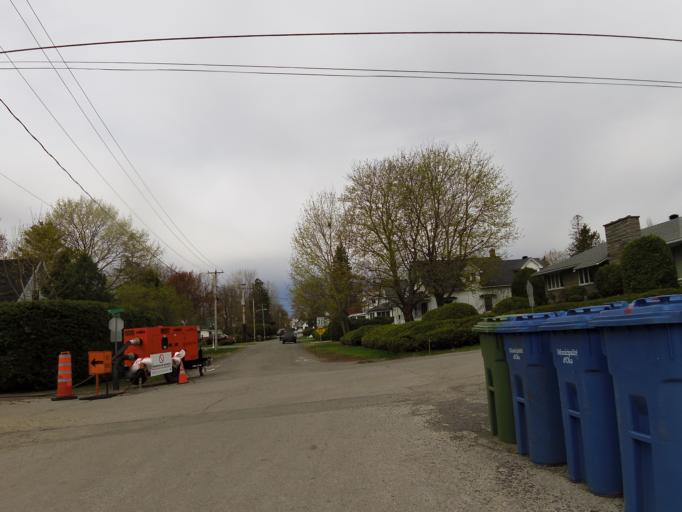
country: CA
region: Quebec
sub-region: Laurentides
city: Oka
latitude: 45.4622
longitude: -74.0832
